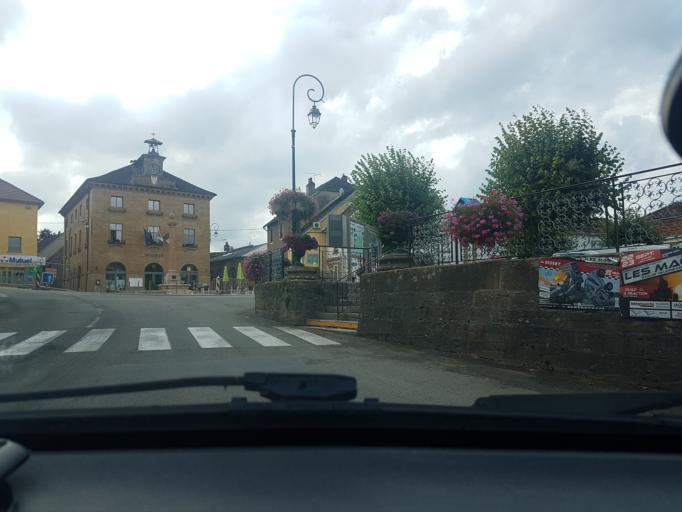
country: FR
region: Franche-Comte
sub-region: Departement du Doubs
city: Rougemont
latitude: 47.4801
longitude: 6.3548
